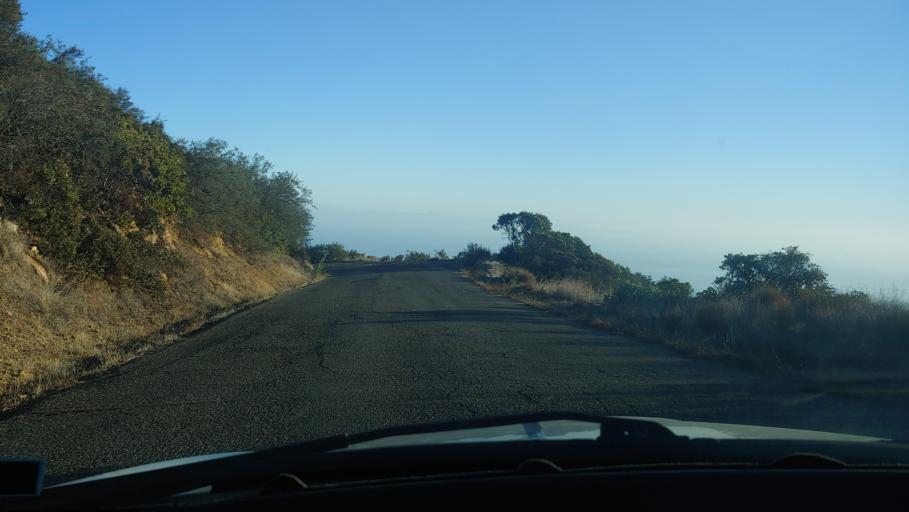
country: US
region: California
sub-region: Santa Barbara County
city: Mission Canyon
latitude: 34.5084
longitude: -119.7689
